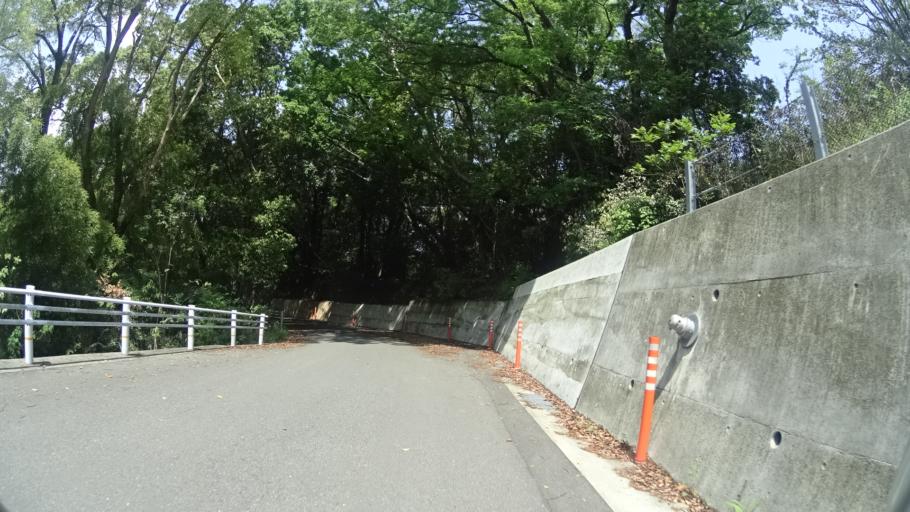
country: JP
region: Tokushima
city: Tokushima-shi
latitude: 34.0676
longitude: 134.5143
